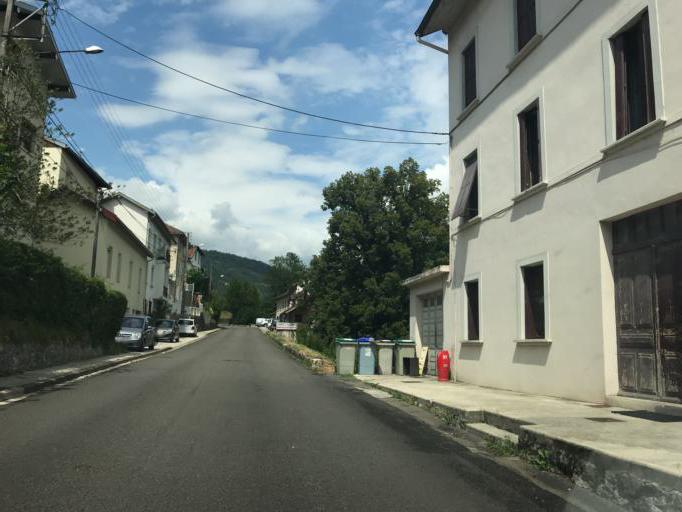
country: FR
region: Franche-Comte
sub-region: Departement du Jura
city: Saint-Claude
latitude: 46.4018
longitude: 5.8650
